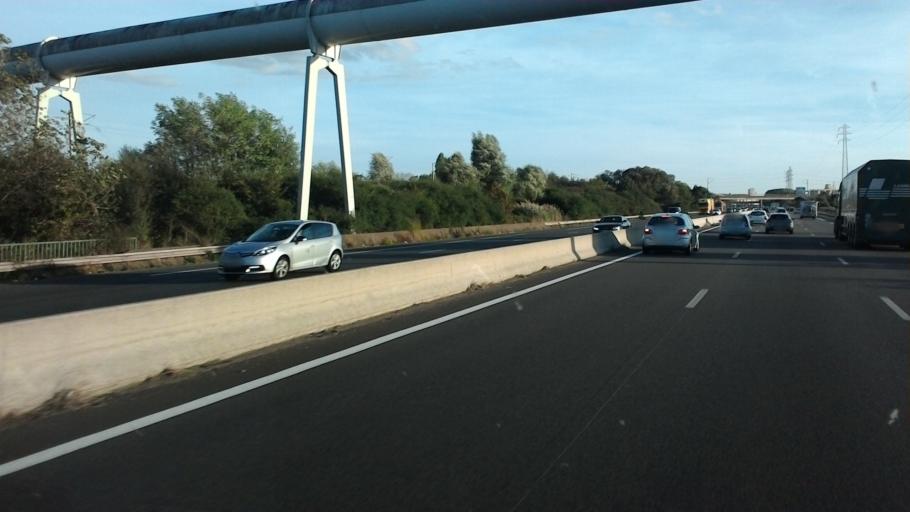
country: FR
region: Lorraine
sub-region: Departement de la Moselle
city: Saint-Julien-les-Metz
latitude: 49.1584
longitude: 6.1824
